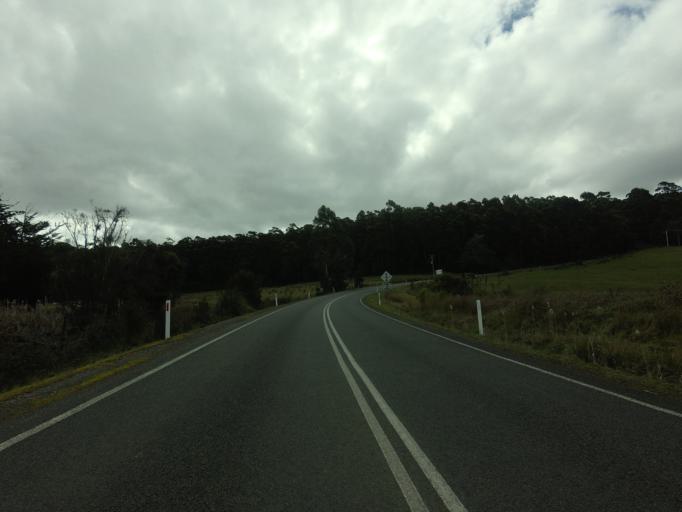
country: AU
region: Tasmania
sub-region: Huon Valley
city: Geeveston
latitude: -43.4119
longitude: 146.9541
